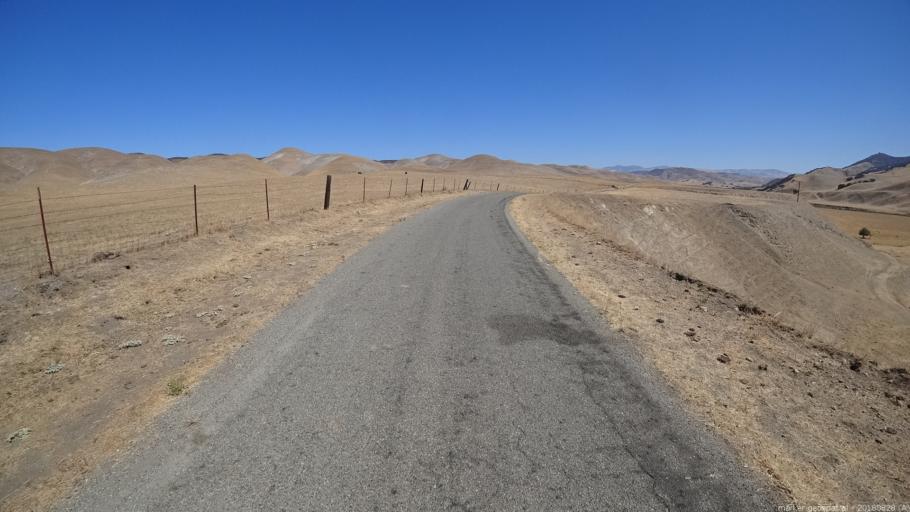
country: US
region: California
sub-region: San Luis Obispo County
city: San Miguel
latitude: 36.0529
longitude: -120.8126
